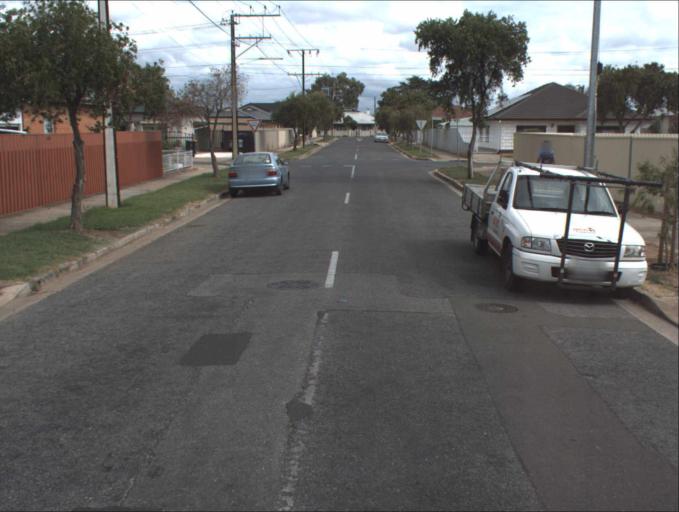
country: AU
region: South Australia
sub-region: Port Adelaide Enfield
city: Blair Athol
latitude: -34.8670
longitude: 138.5875
